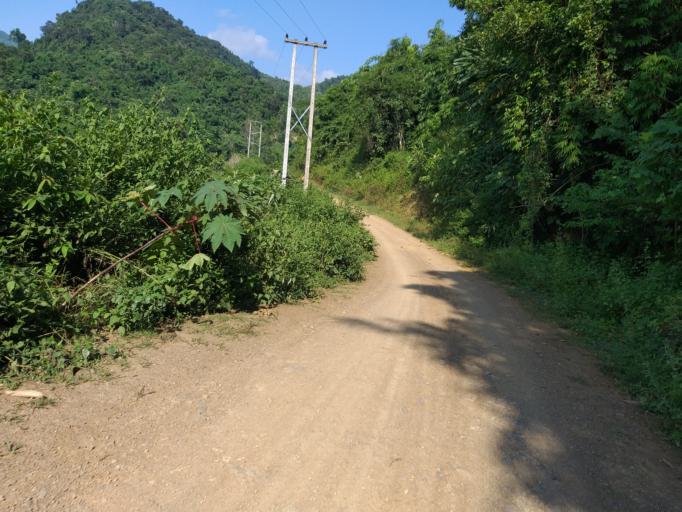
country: LA
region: Phongsali
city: Khoa
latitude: 21.1947
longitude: 102.6436
